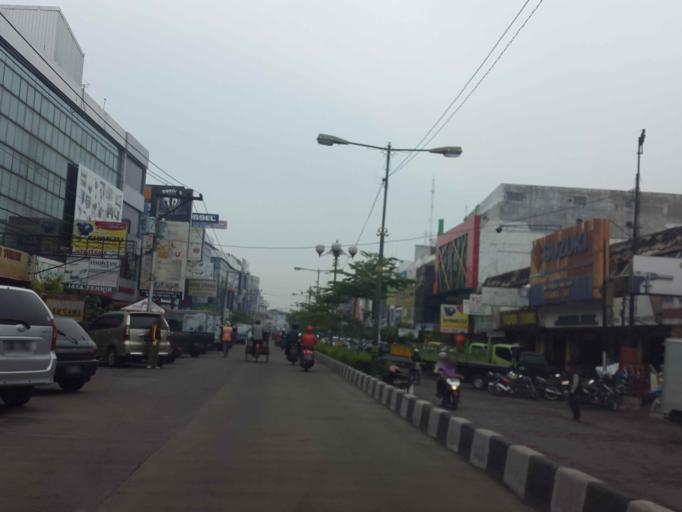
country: ID
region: Central Java
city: Semarang
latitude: -6.9702
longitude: 110.4299
